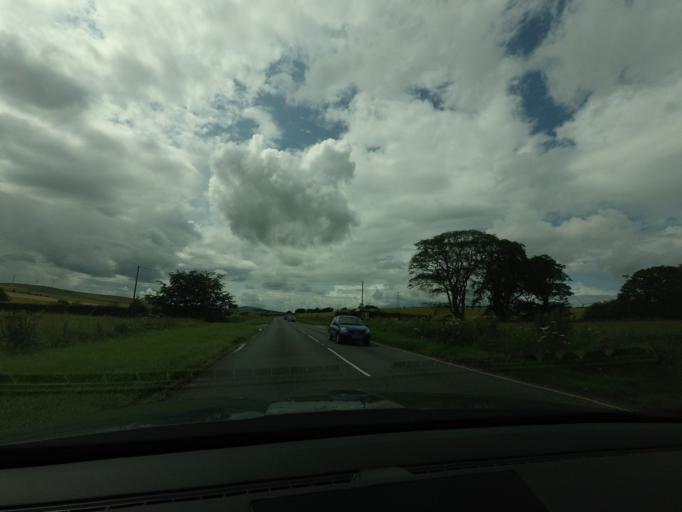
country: GB
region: Scotland
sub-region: Aberdeenshire
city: Whitehills
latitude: 57.6582
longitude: -2.6012
